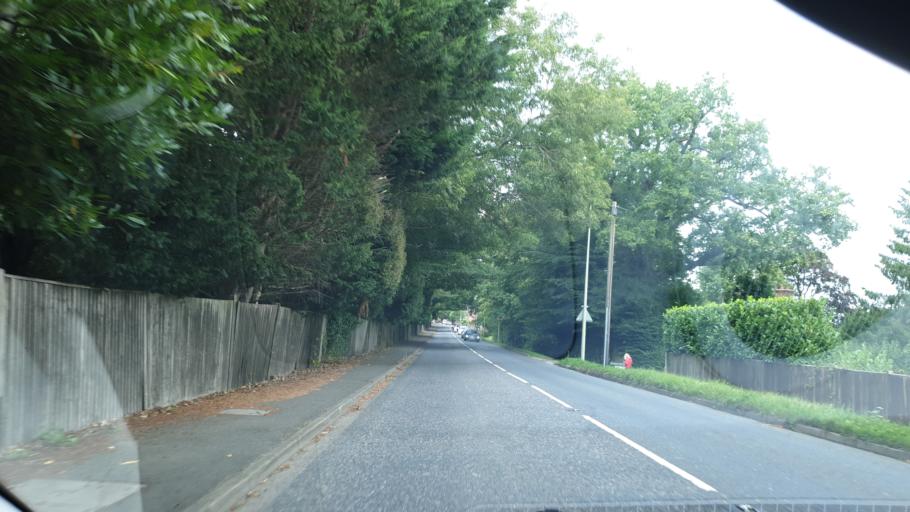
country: GB
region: England
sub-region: East Sussex
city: Forest Row
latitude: 51.0921
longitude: 0.0322
